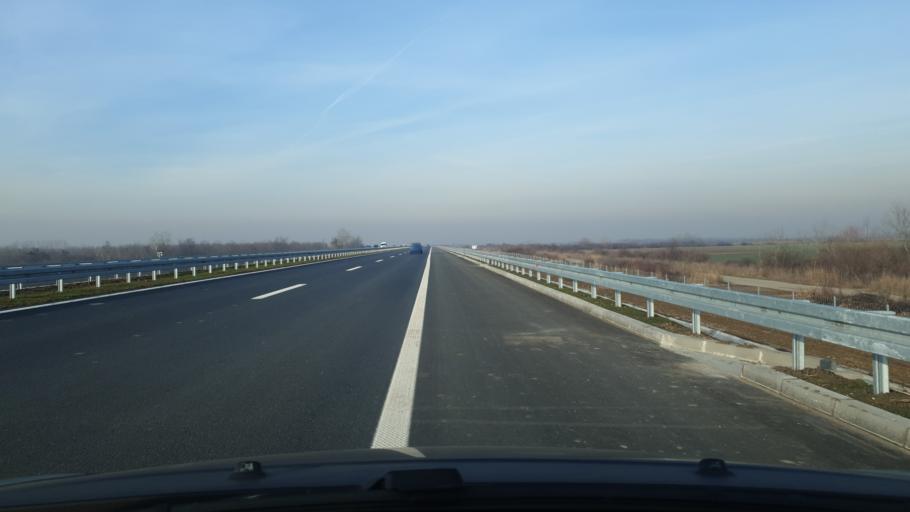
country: RS
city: Umka
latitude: 44.7003
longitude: 20.2642
